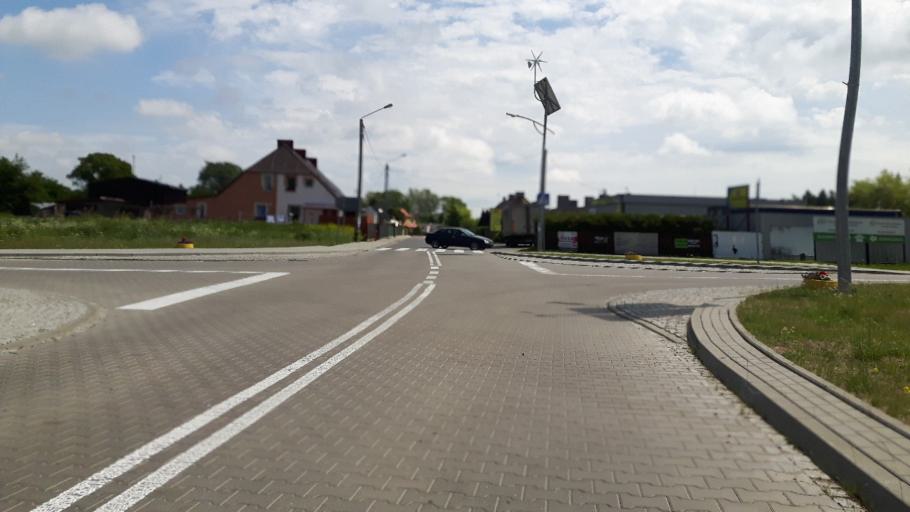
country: PL
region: Pomeranian Voivodeship
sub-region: Powiat wejherowski
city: Choczewo
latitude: 54.7376
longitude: 17.8251
